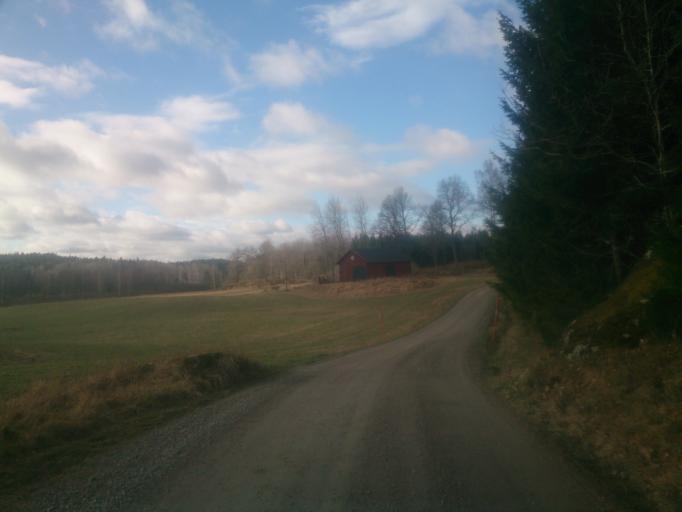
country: SE
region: OEstergoetland
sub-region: Atvidabergs Kommun
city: Atvidaberg
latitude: 58.2345
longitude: 16.1801
